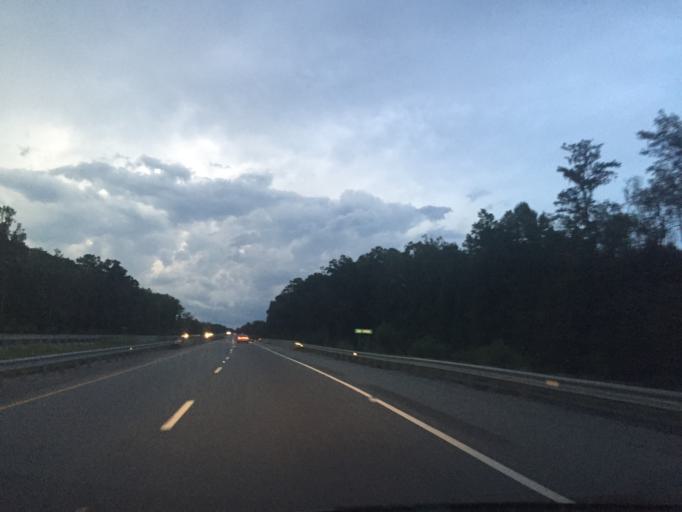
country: US
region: Georgia
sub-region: Liberty County
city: Midway
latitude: 31.8291
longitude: -81.4895
